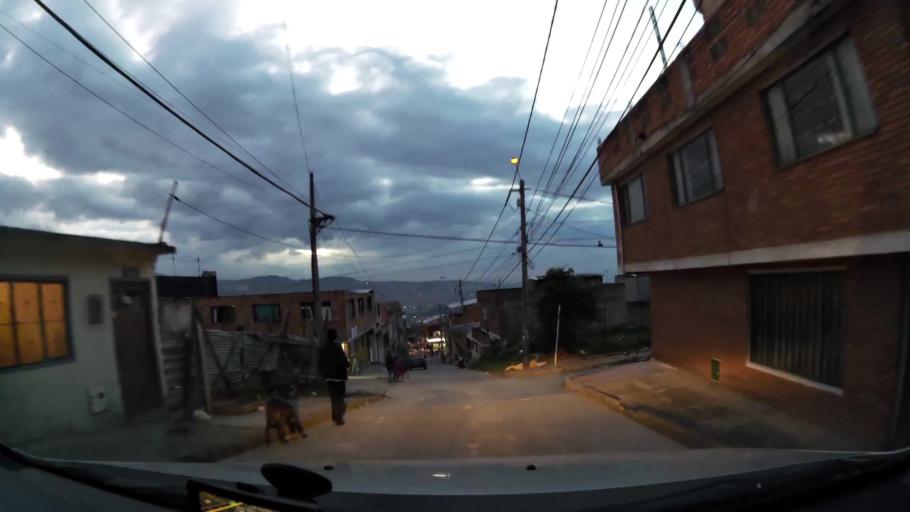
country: CO
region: Bogota D.C.
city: Bogota
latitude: 4.5455
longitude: -74.0827
